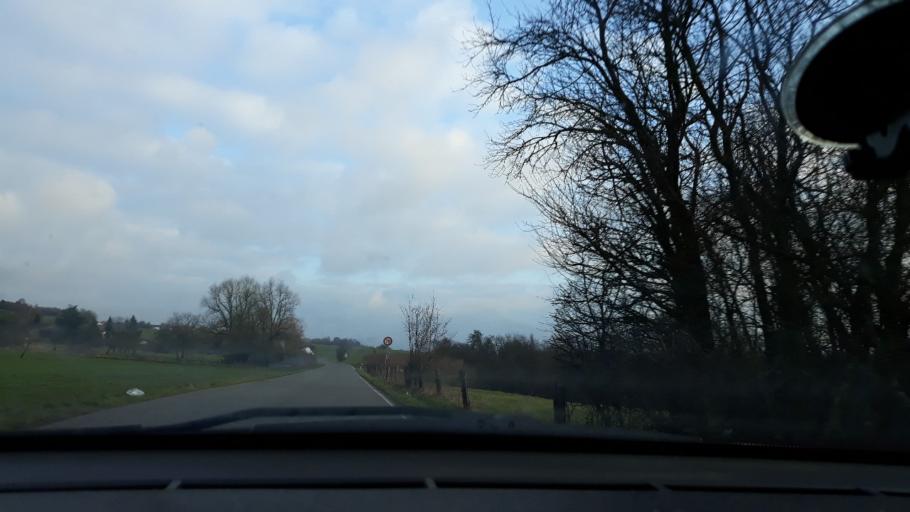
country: DE
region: Saarland
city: Blieskastel
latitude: 49.2101
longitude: 7.2093
